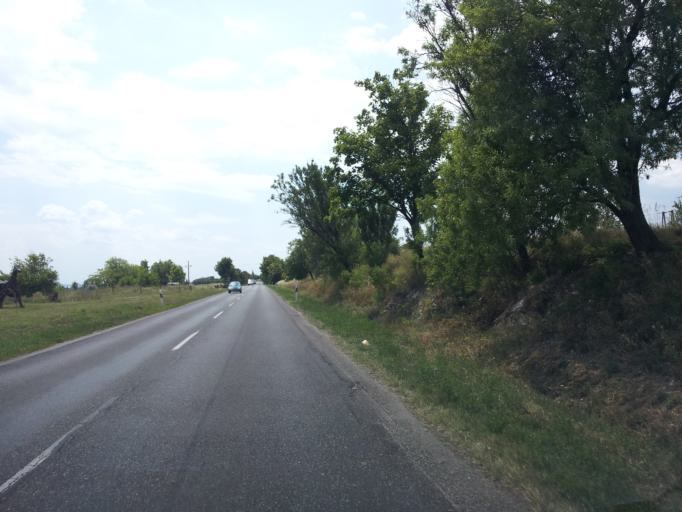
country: HU
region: Veszprem
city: Balatonfured
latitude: 46.9235
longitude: 17.8262
